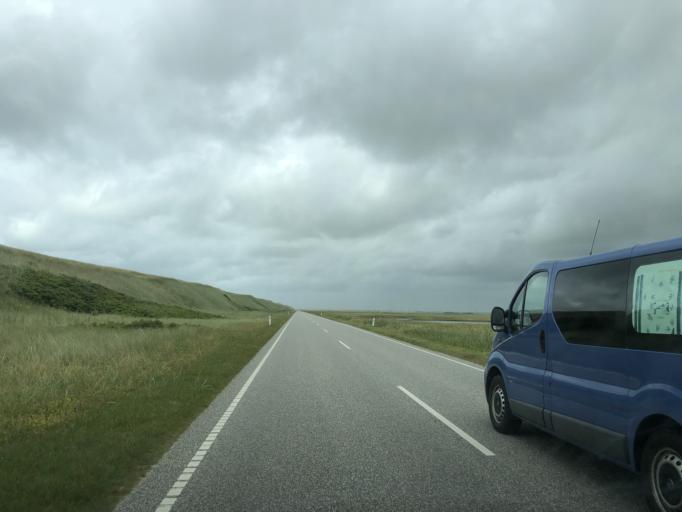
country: DK
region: Central Jutland
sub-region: Lemvig Kommune
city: Harboore
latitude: 56.4167
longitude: 8.1229
